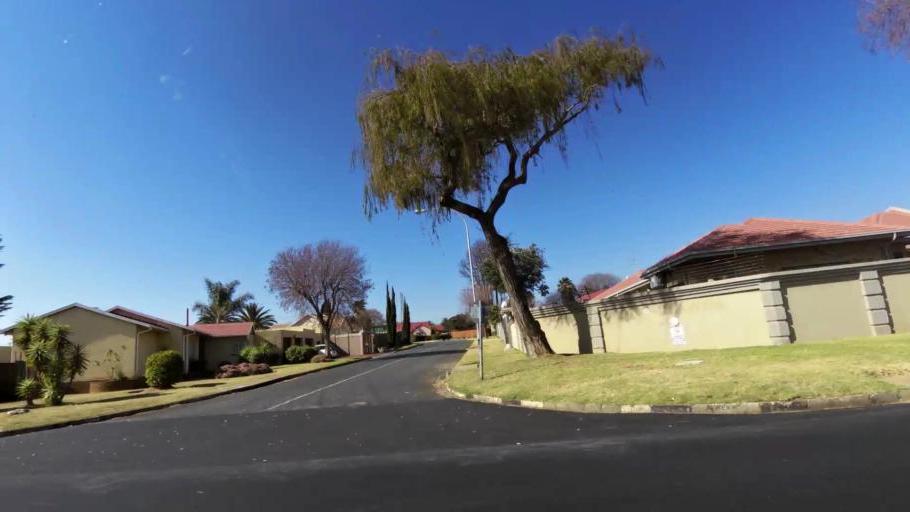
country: ZA
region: Gauteng
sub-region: City of Johannesburg Metropolitan Municipality
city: Johannesburg
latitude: -26.2462
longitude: 28.0001
